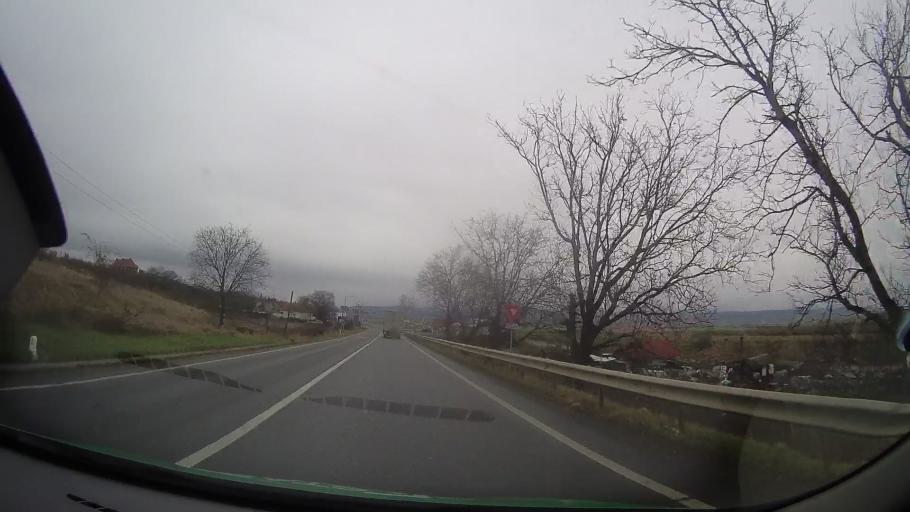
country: RO
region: Mures
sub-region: Comuna Breaza
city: Breaza
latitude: 46.7610
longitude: 24.6616
